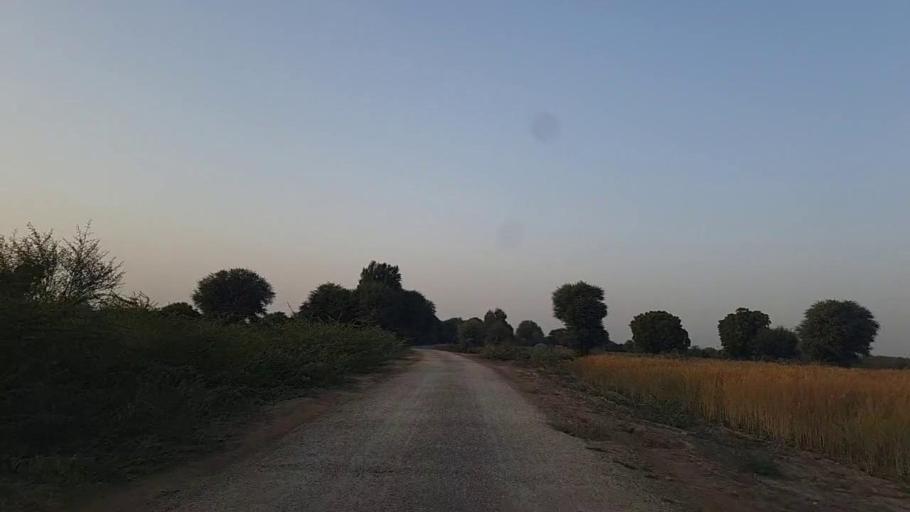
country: PK
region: Sindh
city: Naukot
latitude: 24.6989
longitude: 69.2733
